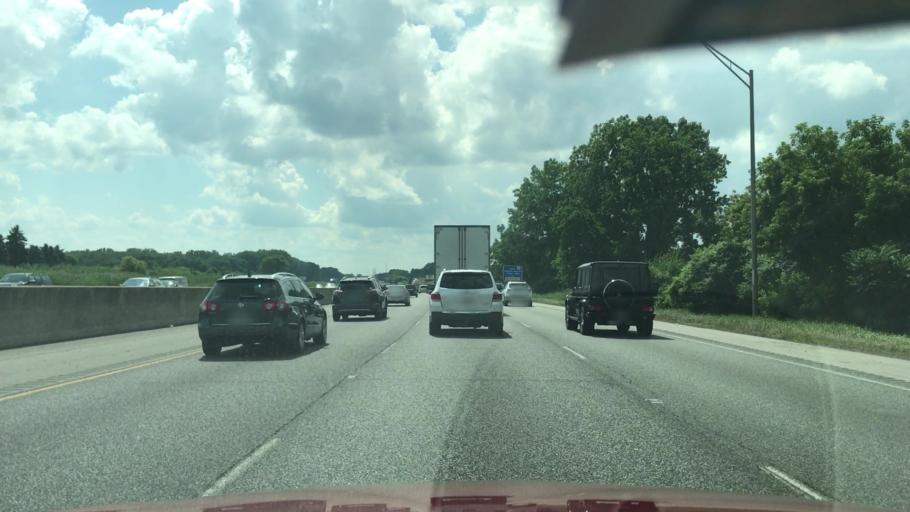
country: US
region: Indiana
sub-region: Porter County
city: Ogden Dunes
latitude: 41.6014
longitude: -87.1832
